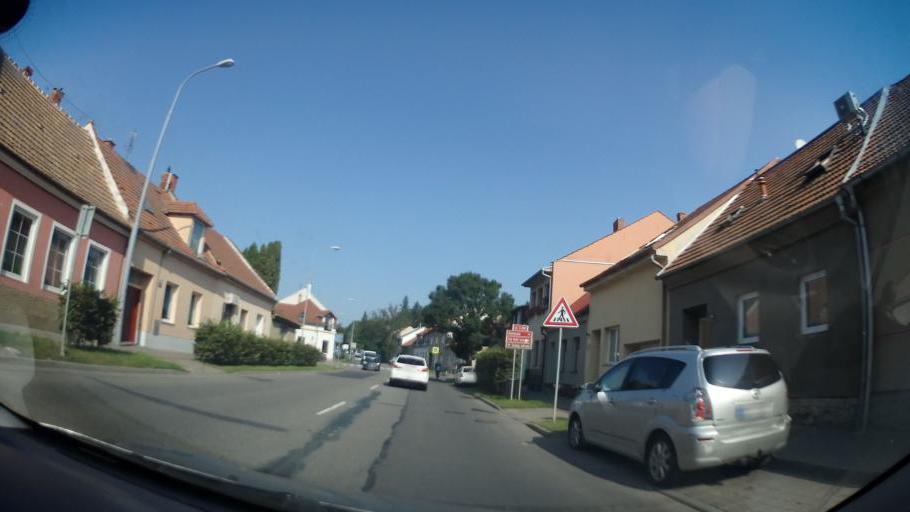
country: CZ
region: South Moravian
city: Troubsko
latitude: 49.2275
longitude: 16.5342
